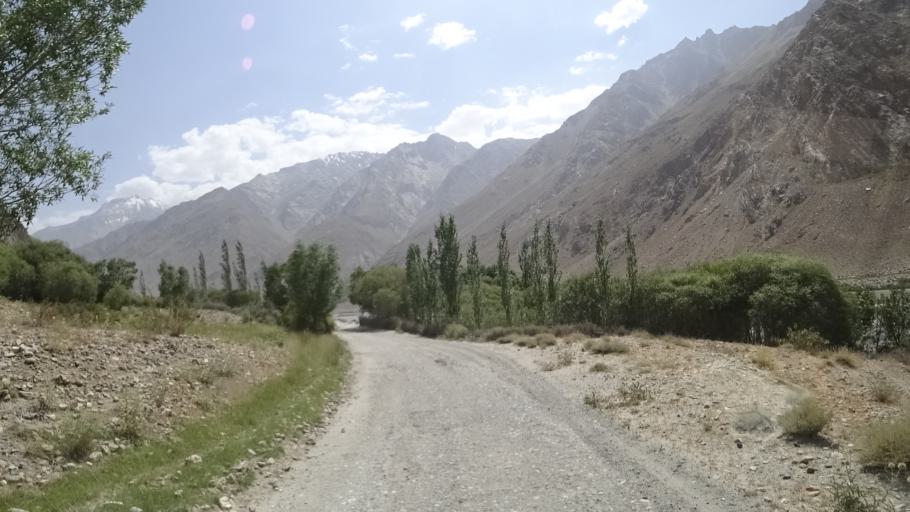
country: TJ
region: Gorno-Badakhshan
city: Ishqoshim
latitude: 36.9761
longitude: 71.4692
